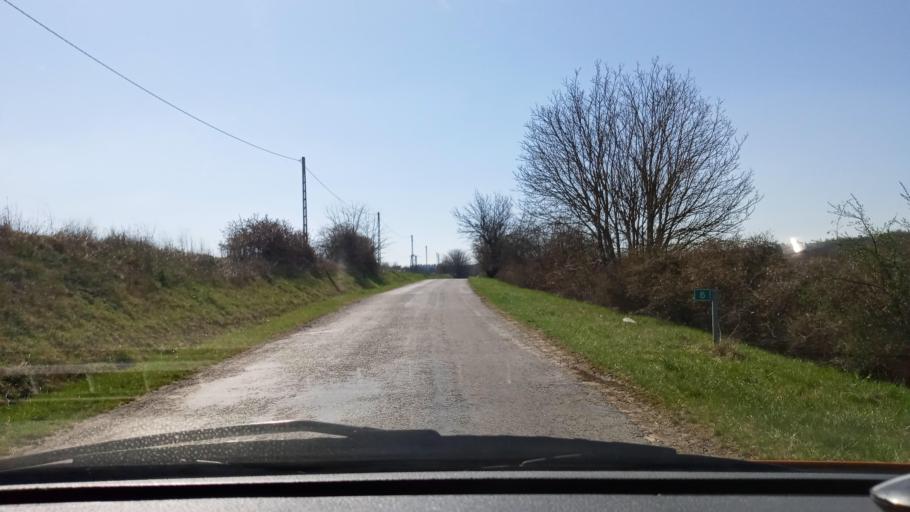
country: HU
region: Baranya
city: Kozarmisleny
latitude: 46.0398
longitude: 18.3860
